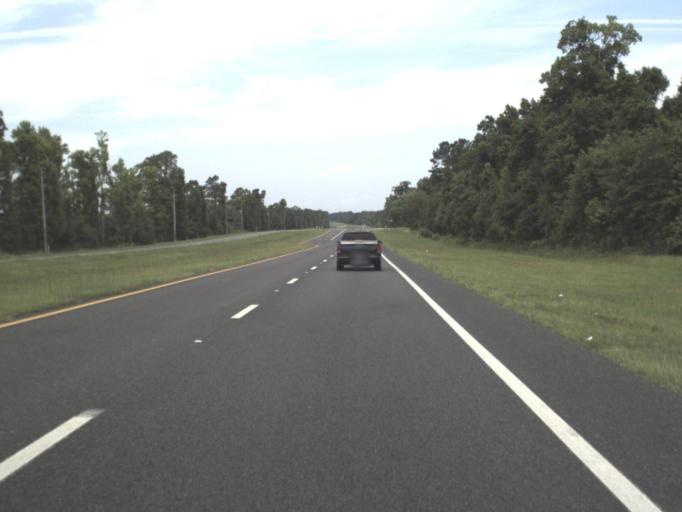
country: US
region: Florida
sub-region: Alachua County
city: Hawthorne
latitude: 29.5993
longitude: -82.1286
